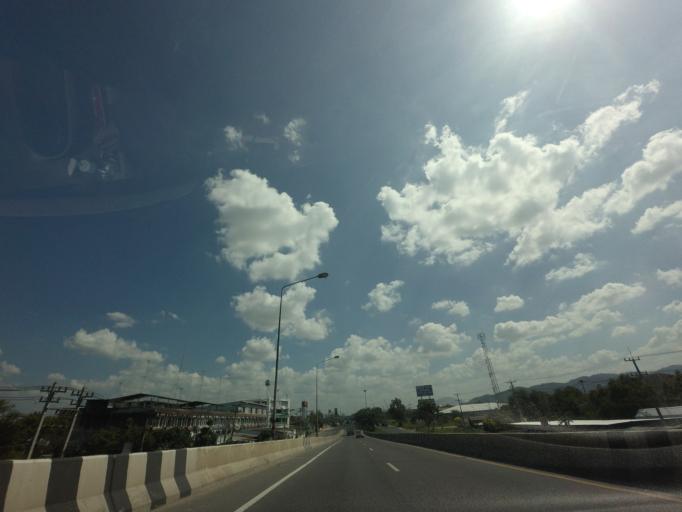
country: TH
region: Chon Buri
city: Ban Bueng
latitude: 13.3159
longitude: 101.1045
